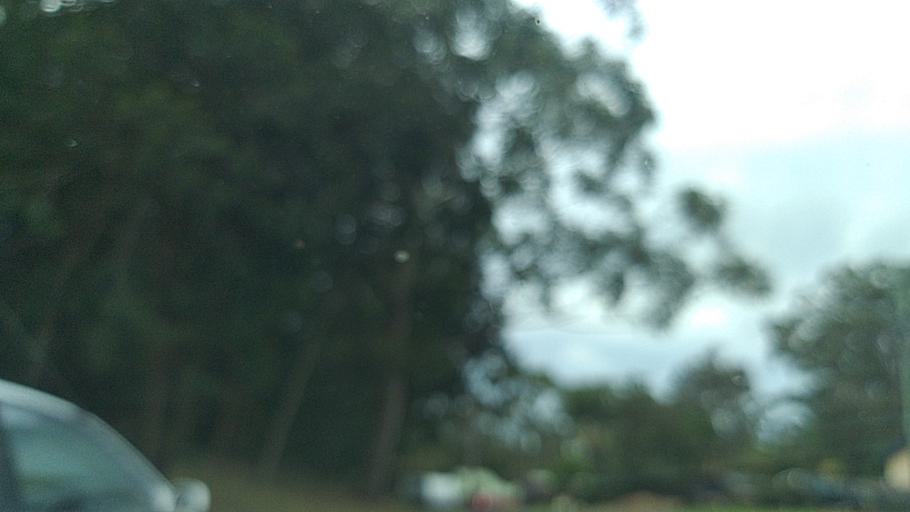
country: AU
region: New South Wales
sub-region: Wollongong
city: Bulli
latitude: -34.3006
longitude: 150.9298
